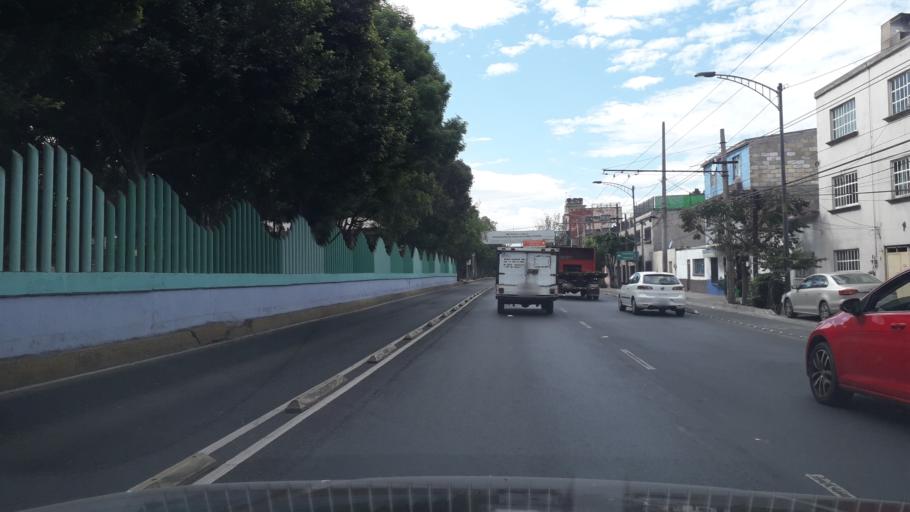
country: MX
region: Mexico City
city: Venustiano Carranza
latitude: 19.4659
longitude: -99.1037
